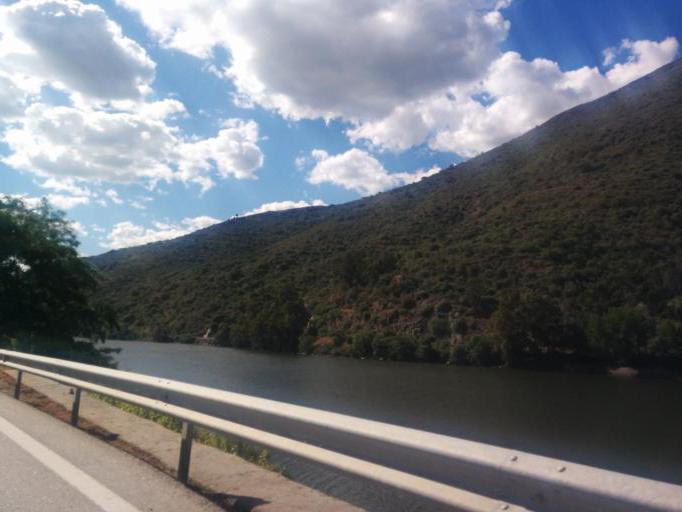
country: PT
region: Viseu
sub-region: Armamar
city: Armamar
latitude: 41.1428
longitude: -7.7071
